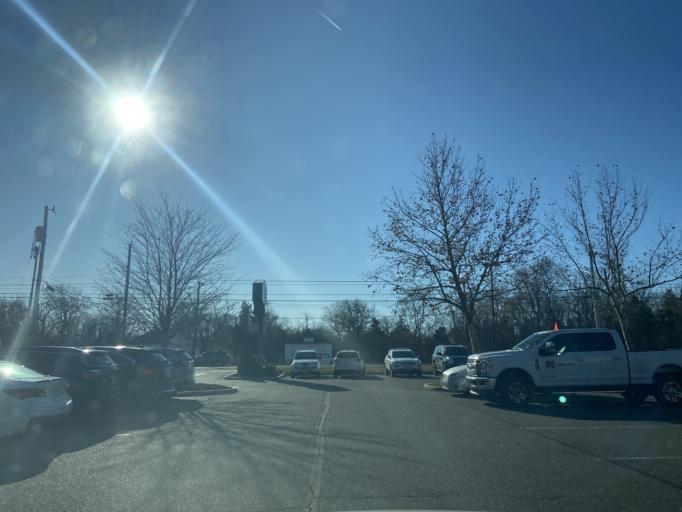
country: US
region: New Jersey
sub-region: Cumberland County
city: Vineland
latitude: 39.4886
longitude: -75.0657
